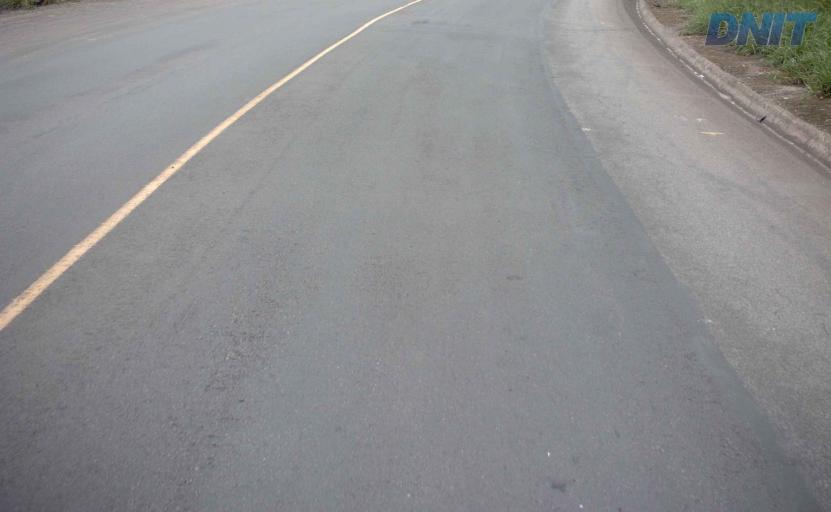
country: BR
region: Minas Gerais
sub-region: Timoteo
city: Timoteo
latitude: -19.5392
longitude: -42.6778
